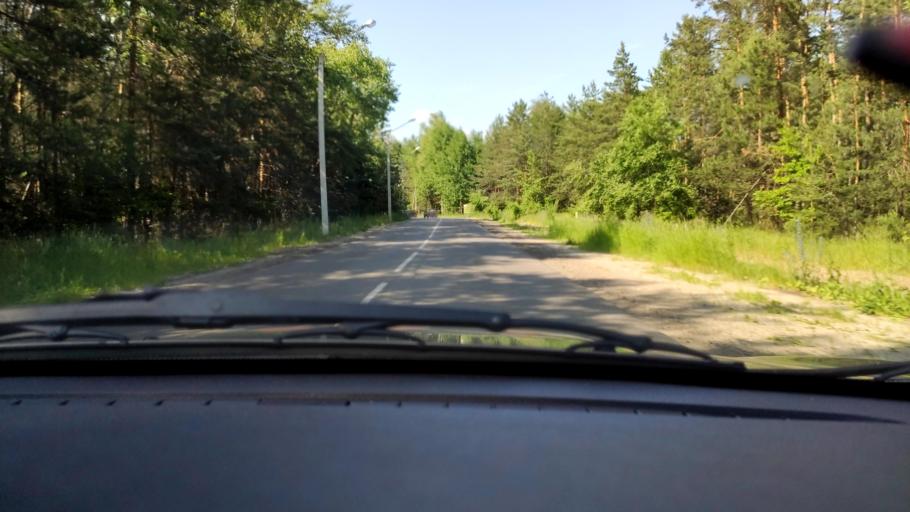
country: RU
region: Voronezj
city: Somovo
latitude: 51.7113
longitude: 39.3266
